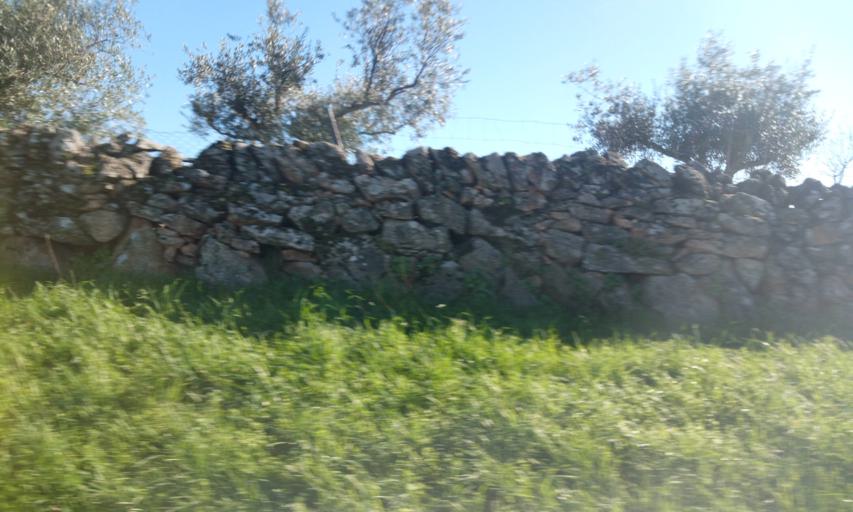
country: PT
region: Guarda
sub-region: Fornos de Algodres
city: Fornos de Algodres
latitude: 40.5270
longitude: -7.5896
